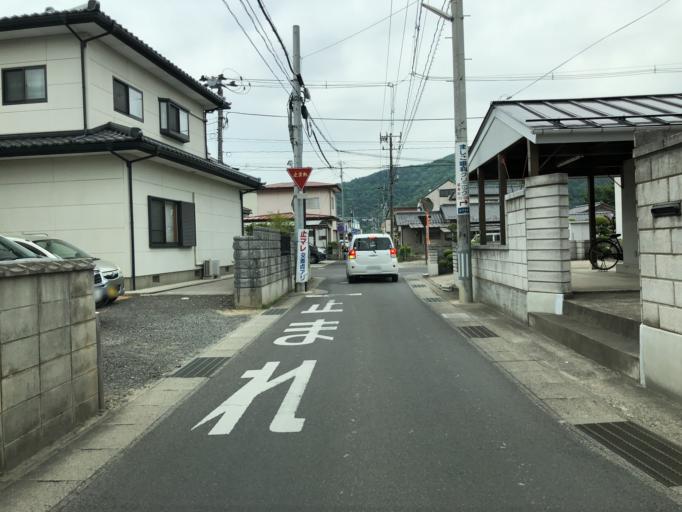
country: JP
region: Fukushima
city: Fukushima-shi
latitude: 37.7864
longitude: 140.4795
